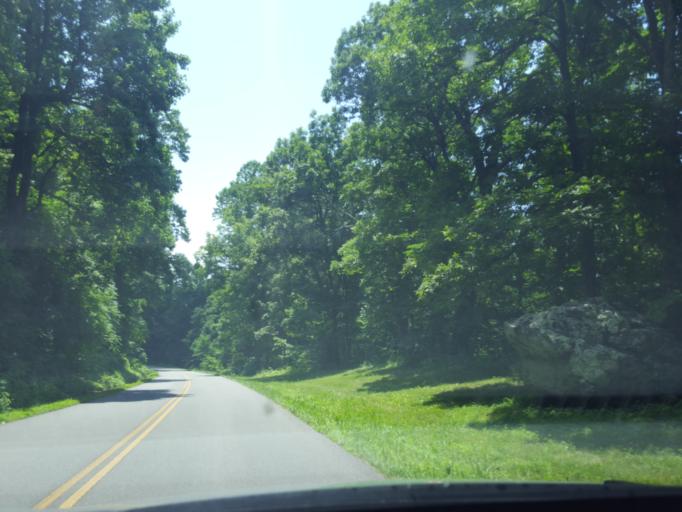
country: US
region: Virginia
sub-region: Nelson County
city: Nellysford
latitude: 37.9189
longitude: -78.9687
